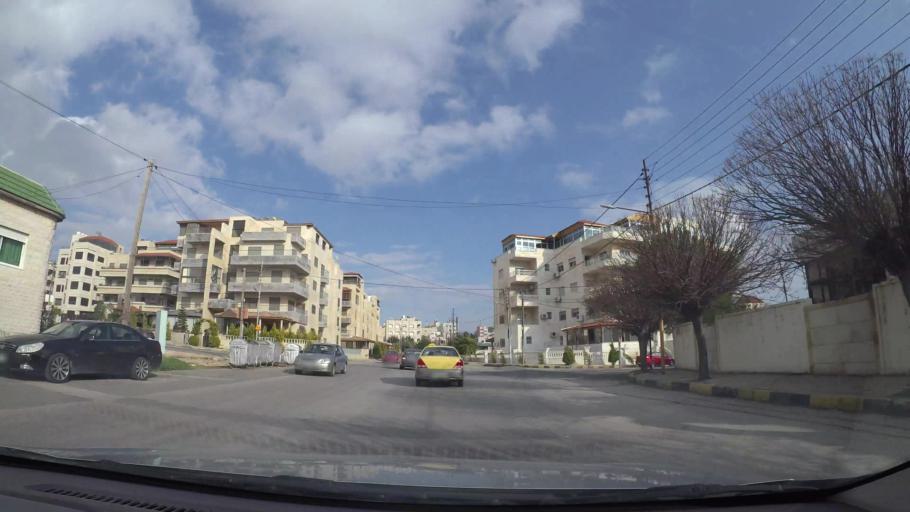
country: JO
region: Amman
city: Wadi as Sir
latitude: 31.9818
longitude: 35.8433
